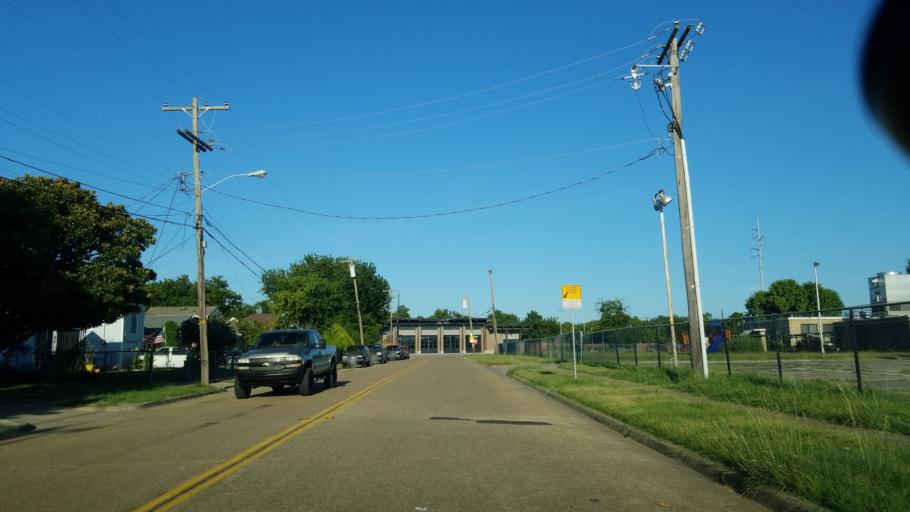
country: US
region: Texas
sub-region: Dallas County
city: Balch Springs
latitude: 32.7747
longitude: -96.7016
